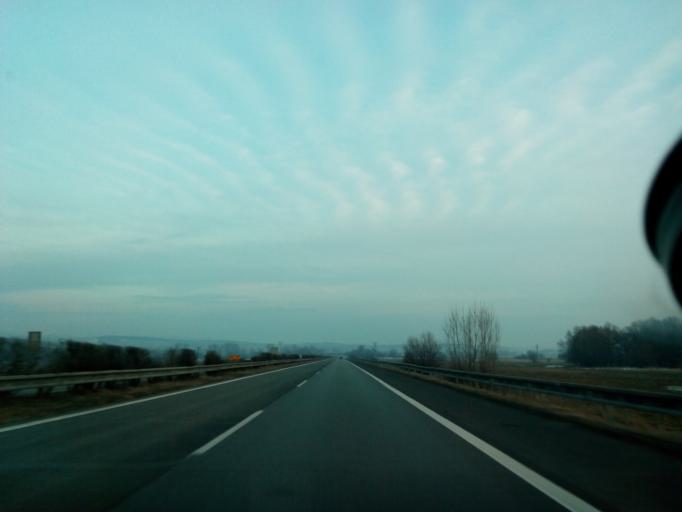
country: SK
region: Kosicky
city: Kosice
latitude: 48.8528
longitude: 21.2769
